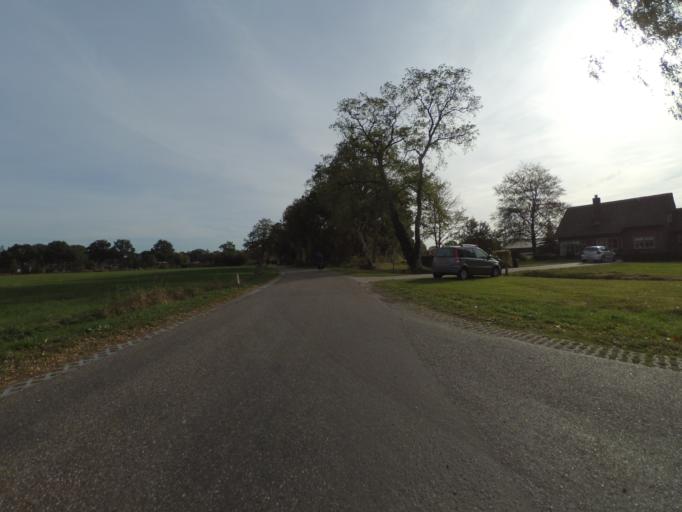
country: NL
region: Overijssel
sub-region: Gemeente Raalte
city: Raalte
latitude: 52.3590
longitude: 6.3703
